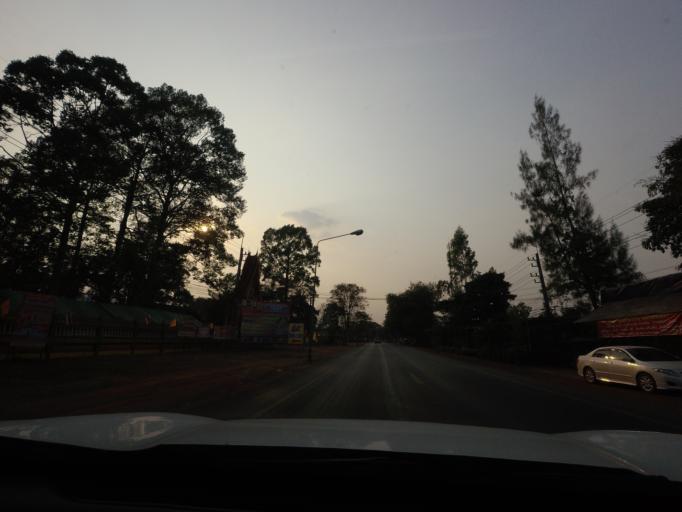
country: TH
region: Nakhon Nayok
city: Pak Phli
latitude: 14.1476
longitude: 101.3422
